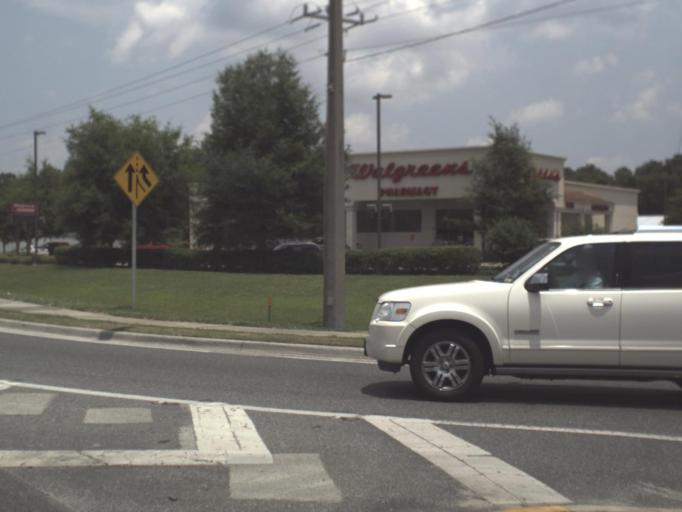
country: US
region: Florida
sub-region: Putnam County
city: Palatka
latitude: 29.6416
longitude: -81.6760
